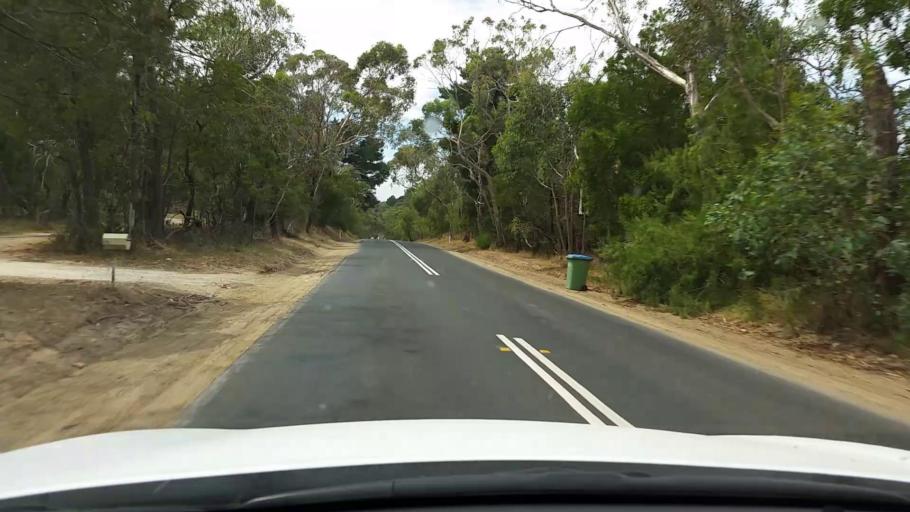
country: AU
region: Victoria
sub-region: Mornington Peninsula
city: Mount Martha
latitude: -38.2906
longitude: 145.0554
